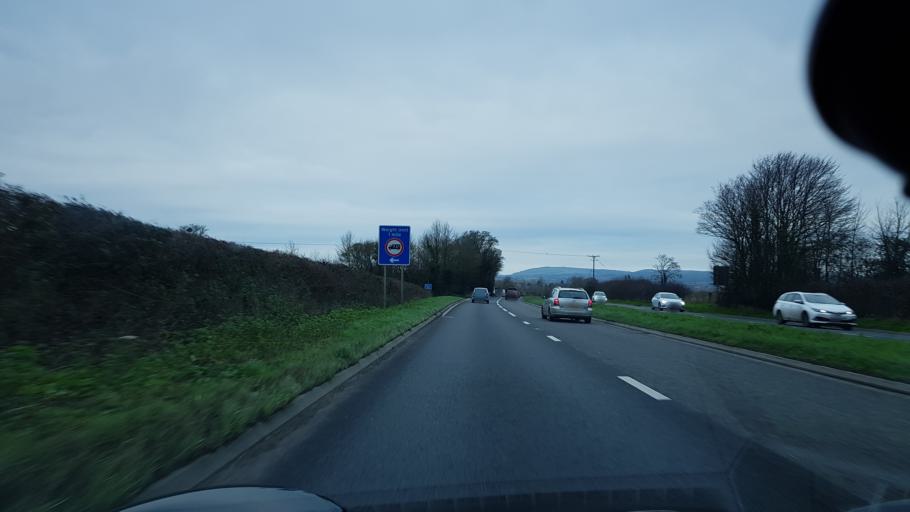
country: GB
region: England
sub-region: Somerset
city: Creech Saint Michael
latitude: 51.0030
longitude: -3.0261
